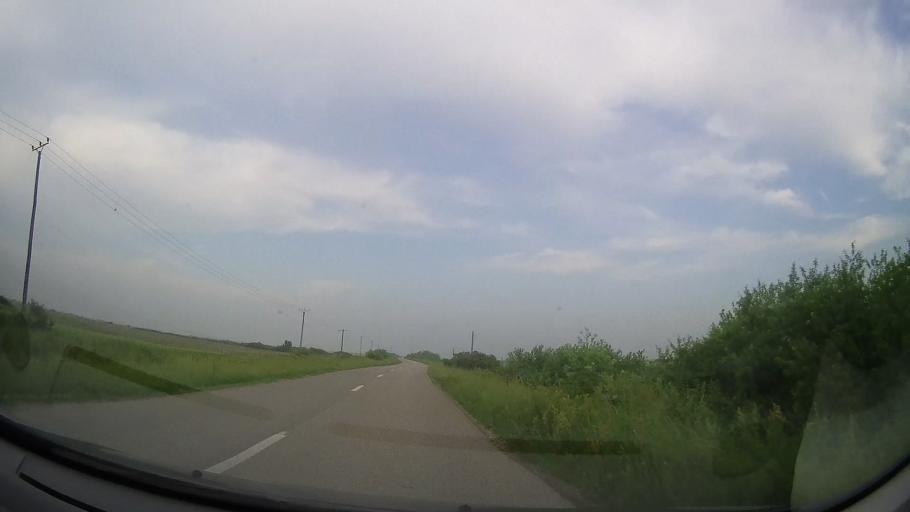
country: RO
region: Timis
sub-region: Comuna Foeni
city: Foeni
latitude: 45.5222
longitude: 20.9154
